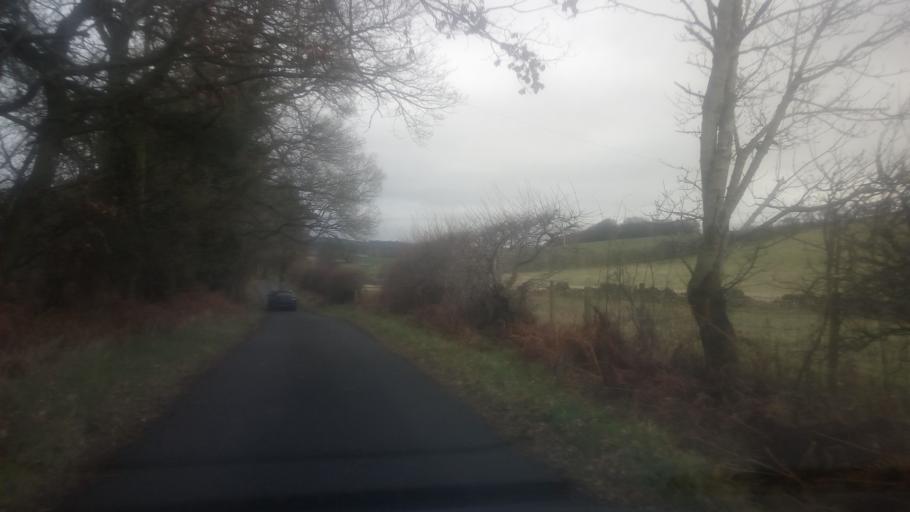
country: GB
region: Scotland
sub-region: The Scottish Borders
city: Jedburgh
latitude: 55.4986
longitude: -2.5407
